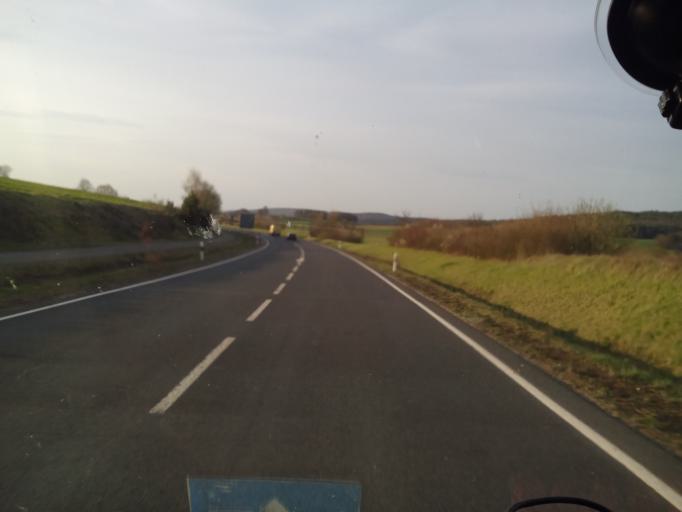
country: DE
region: Bavaria
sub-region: Upper Franconia
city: Reckendorf
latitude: 50.0354
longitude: 10.8247
